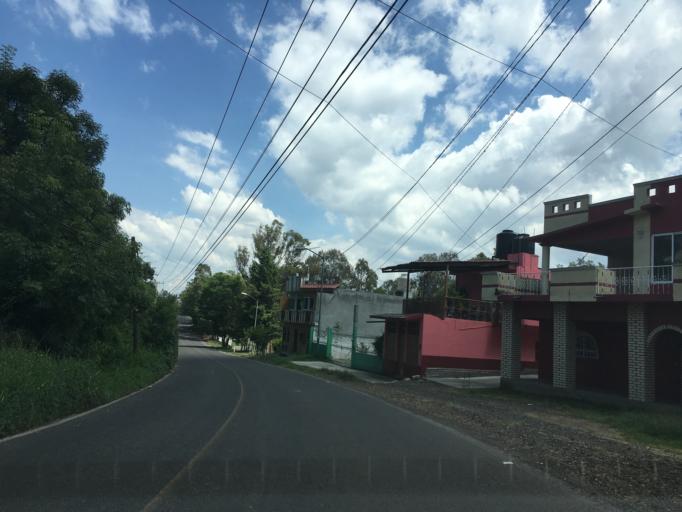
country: MX
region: Michoacan
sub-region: Morelia
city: Morelos
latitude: 19.6404
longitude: -101.2587
